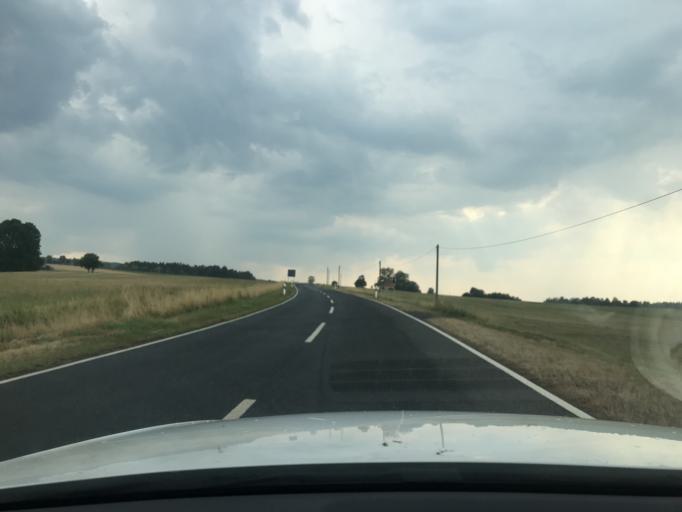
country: DE
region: Bavaria
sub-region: Upper Palatinate
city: Schlammersdorf
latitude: 49.8015
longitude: 11.7282
